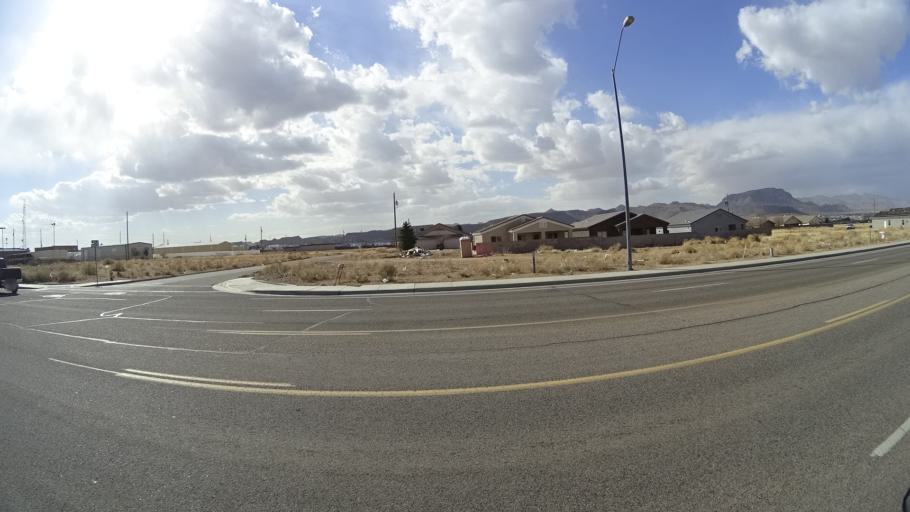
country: US
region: Arizona
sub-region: Mohave County
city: New Kingman-Butler
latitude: 35.2268
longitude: -114.0113
